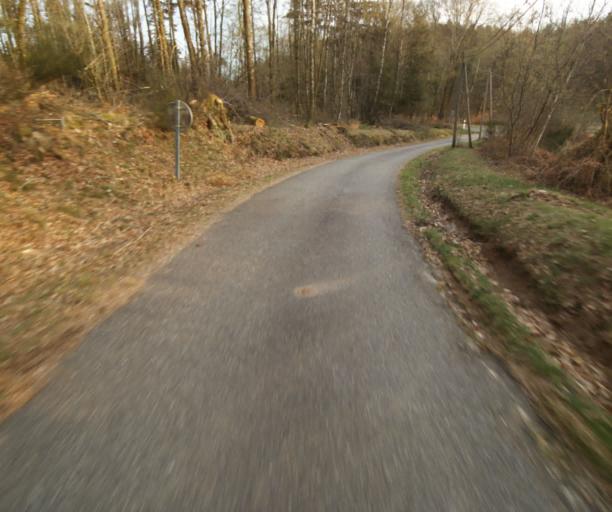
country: FR
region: Limousin
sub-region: Departement de la Correze
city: Argentat
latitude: 45.2433
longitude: 1.9580
